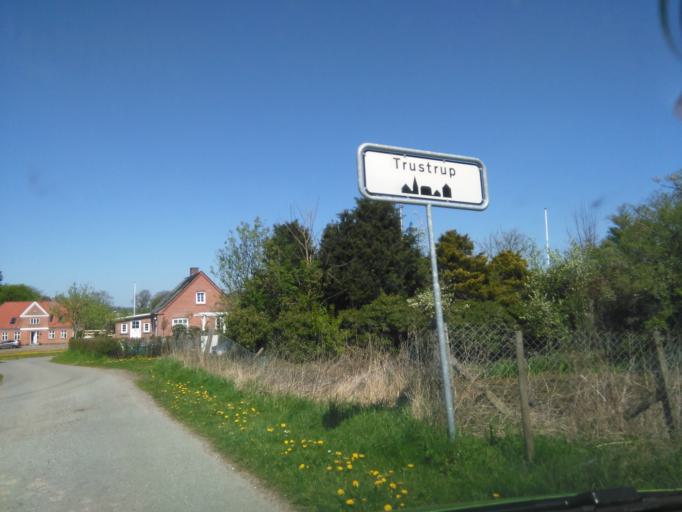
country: DK
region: Central Jutland
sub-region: Odder Kommune
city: Odder
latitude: 55.9022
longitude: 10.0371
